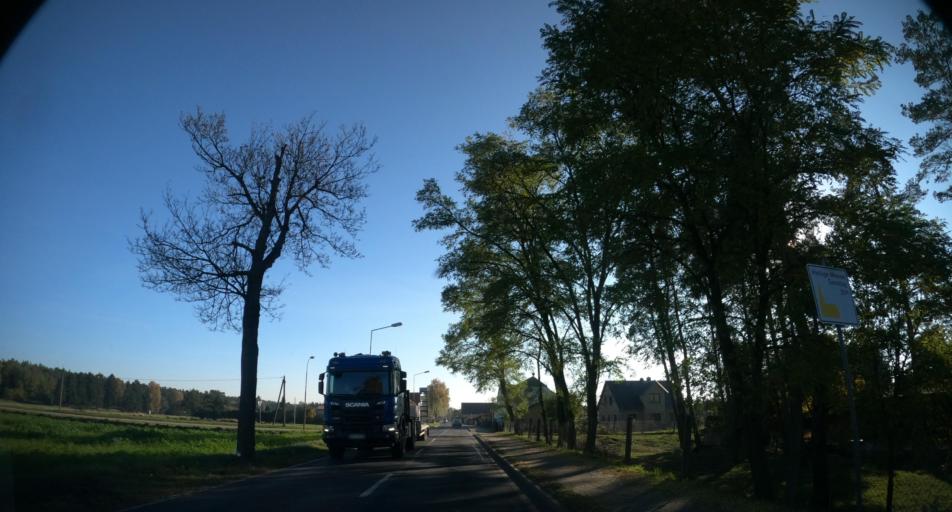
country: DE
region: Mecklenburg-Vorpommern
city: Eggesin
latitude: 53.7098
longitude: 14.0696
